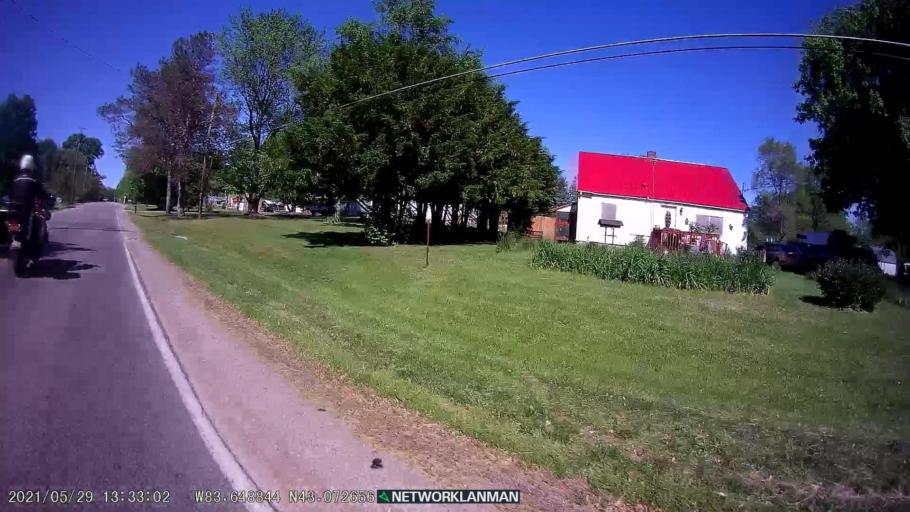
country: US
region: Michigan
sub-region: Genesee County
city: Beecher
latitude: 43.0729
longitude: -83.6487
